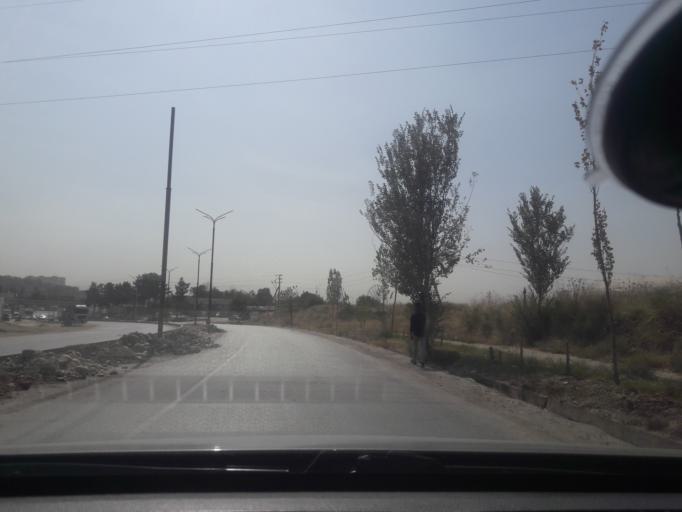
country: TJ
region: Dushanbe
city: Dushanbe
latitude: 38.6049
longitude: 68.7726
